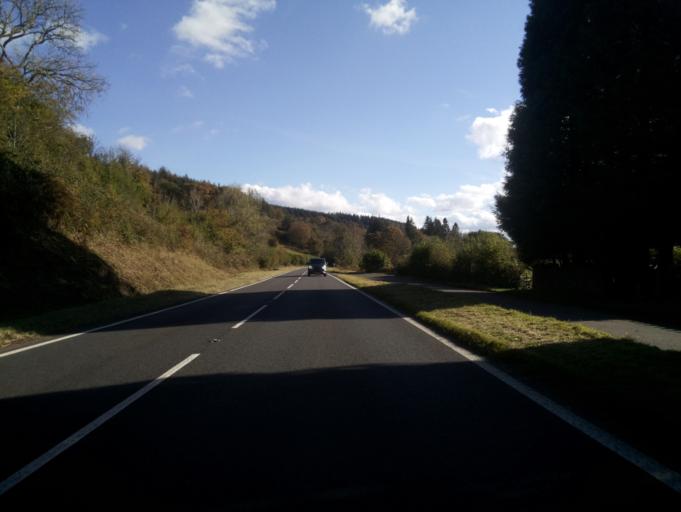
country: GB
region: Wales
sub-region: Merthyr Tydfil County Borough
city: Merthyr Tydfil
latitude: 51.8226
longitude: -3.4468
